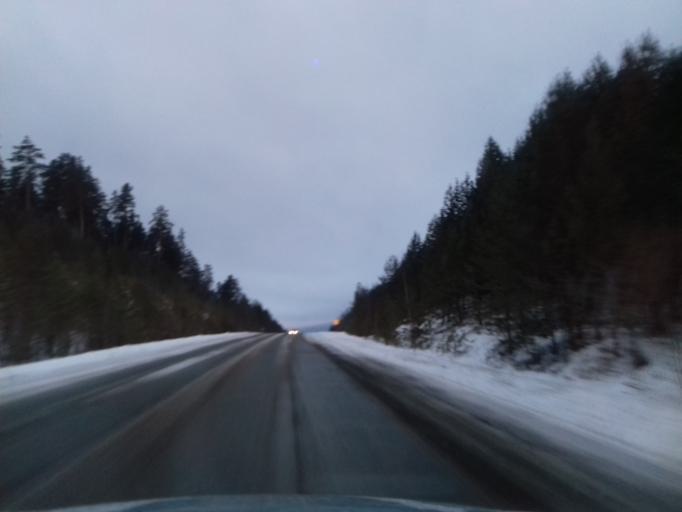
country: RU
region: Bashkortostan
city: Verkhniy Avzyan
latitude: 53.7438
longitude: 57.9168
